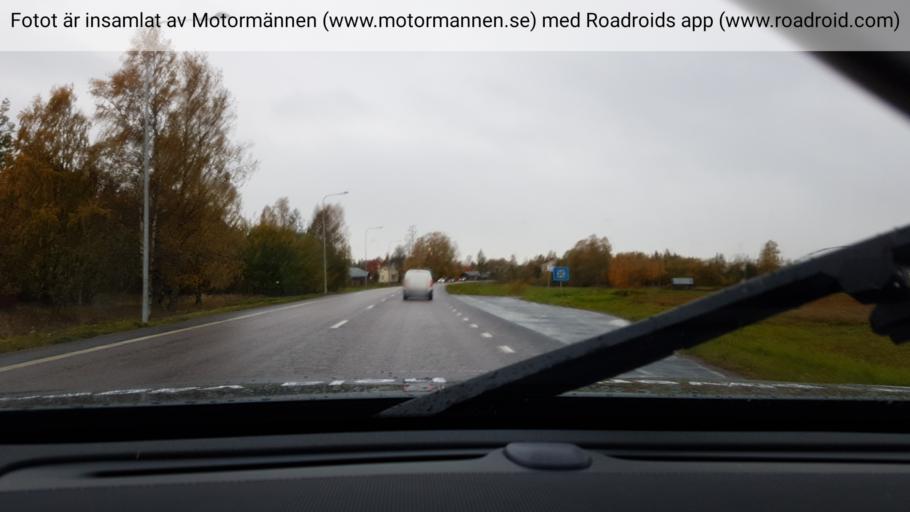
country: SE
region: Norrbotten
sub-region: Lulea Kommun
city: Gammelstad
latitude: 65.5837
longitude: 22.0349
